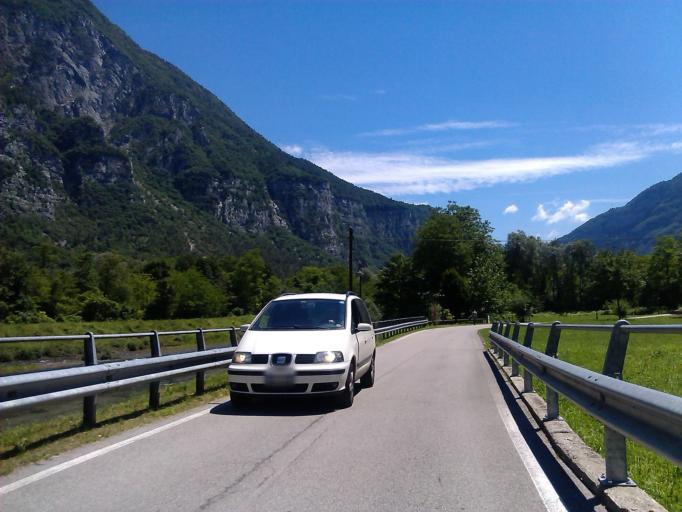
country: IT
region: Trentino-Alto Adige
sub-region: Provincia di Trento
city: Grigno
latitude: 45.9891
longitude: 11.6659
